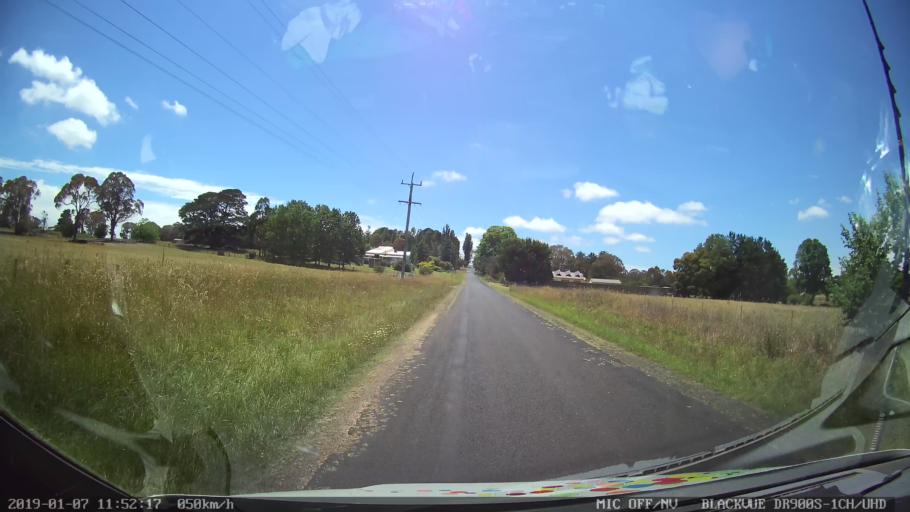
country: AU
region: New South Wales
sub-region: Guyra
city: Guyra
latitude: -30.3084
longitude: 151.6535
